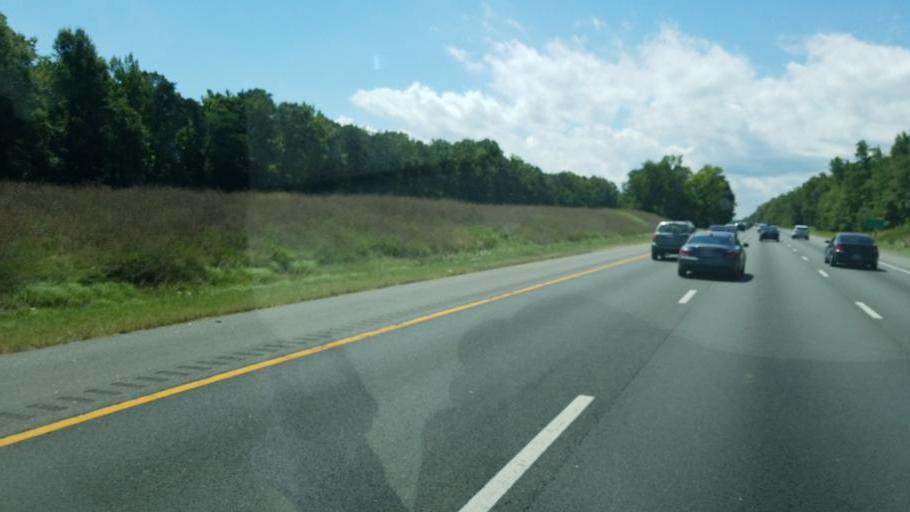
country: US
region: Virginia
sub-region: Spotsylvania County
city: Spotsylvania Courthouse
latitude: 38.1077
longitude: -77.5183
